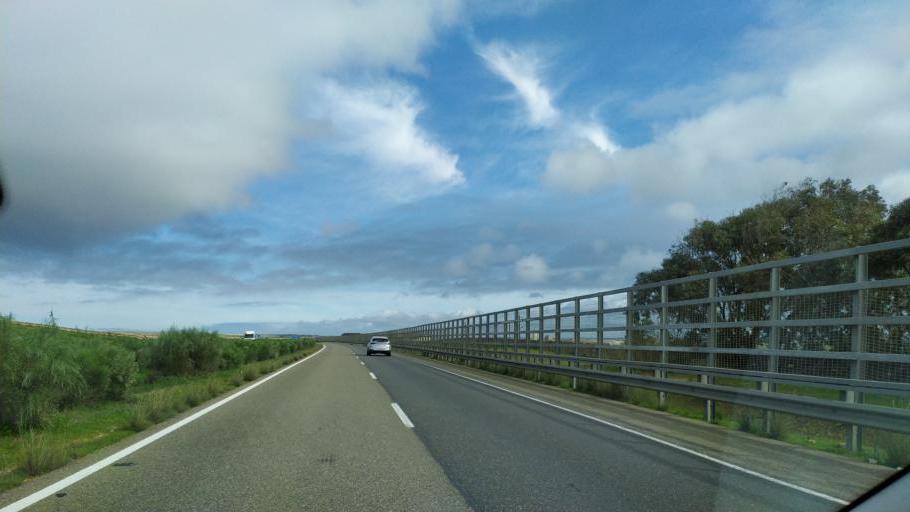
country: MA
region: Gharb-Chrarda-Beni Hssen
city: Sidi Yahia el Gharb
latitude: 34.6016
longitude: -6.4354
